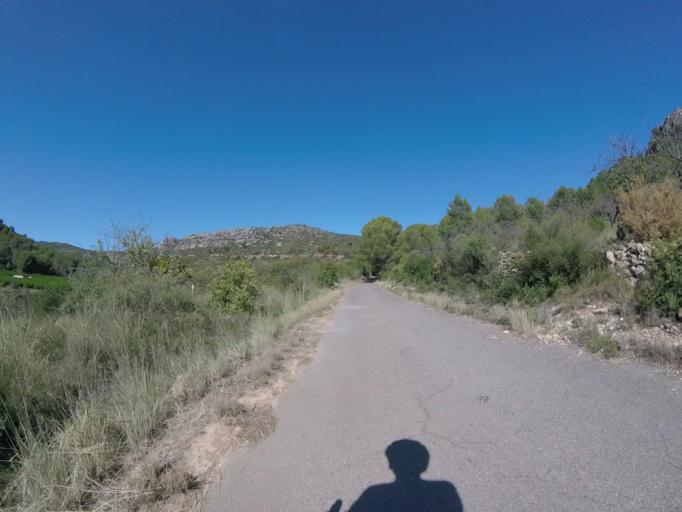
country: ES
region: Valencia
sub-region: Provincia de Castello
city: Orpesa/Oropesa del Mar
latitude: 40.1380
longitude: 0.1029
